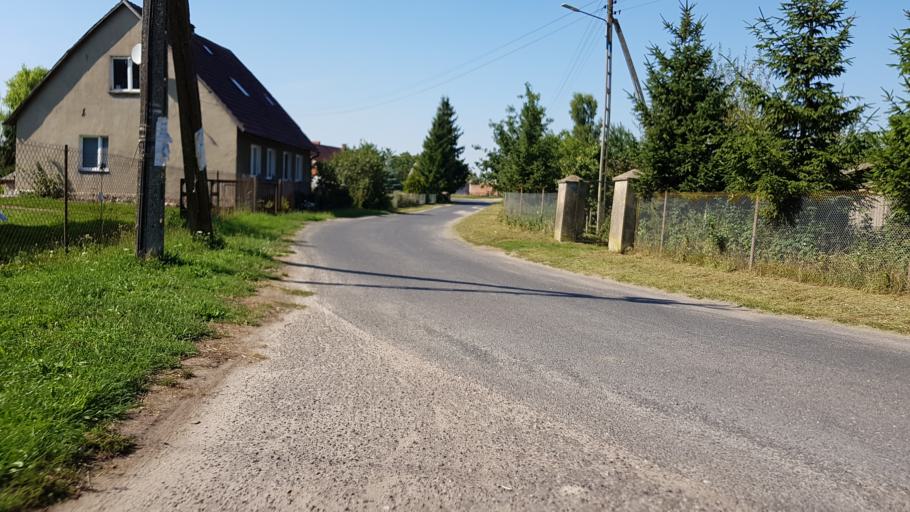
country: PL
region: West Pomeranian Voivodeship
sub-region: Powiat gryfinski
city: Gryfino
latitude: 53.1614
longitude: 14.4832
